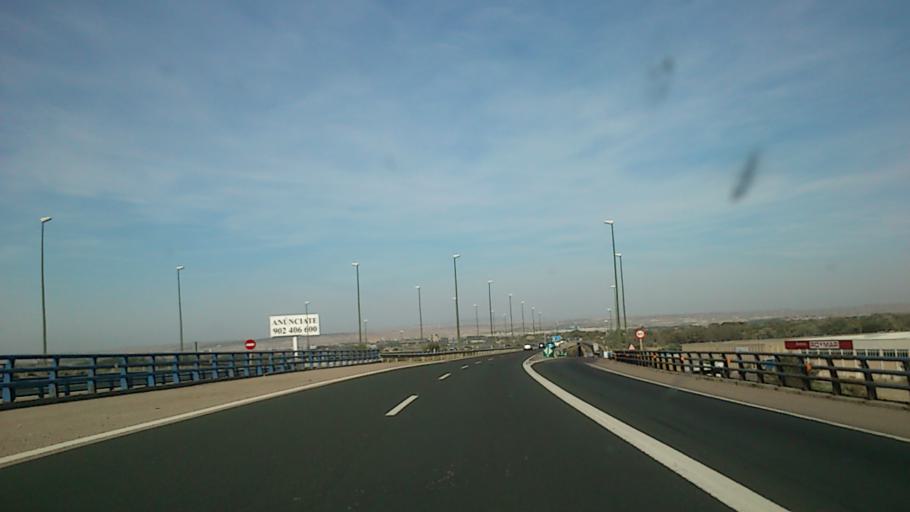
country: ES
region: Aragon
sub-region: Provincia de Zaragoza
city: Zaragoza
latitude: 41.6240
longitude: -0.8529
